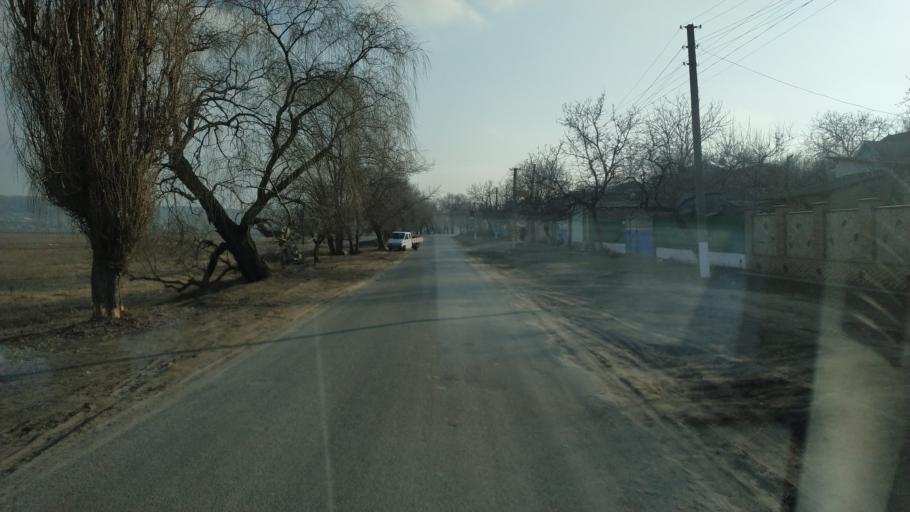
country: MD
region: Hincesti
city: Dancu
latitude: 46.7728
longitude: 28.3463
